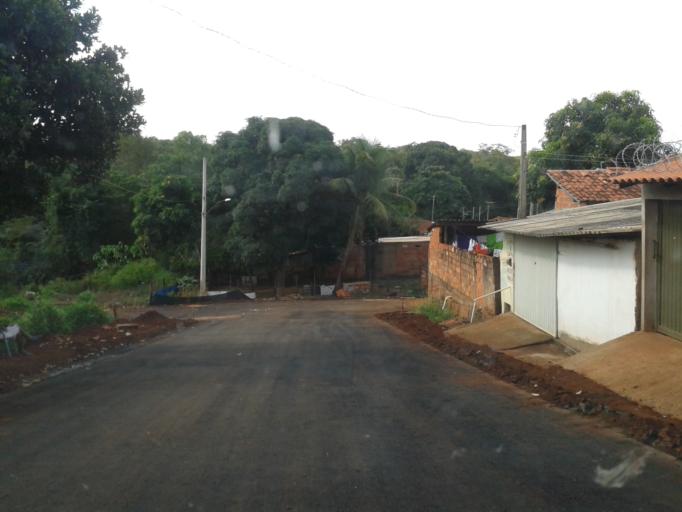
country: BR
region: Minas Gerais
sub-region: Capinopolis
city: Capinopolis
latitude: -18.6821
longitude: -49.5819
